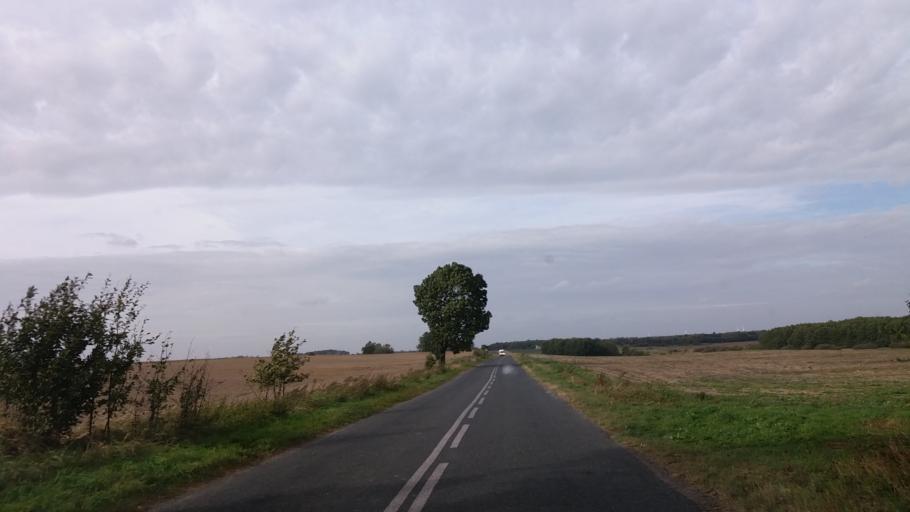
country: PL
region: West Pomeranian Voivodeship
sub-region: Powiat choszczenski
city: Krzecin
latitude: 53.0332
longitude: 15.5016
